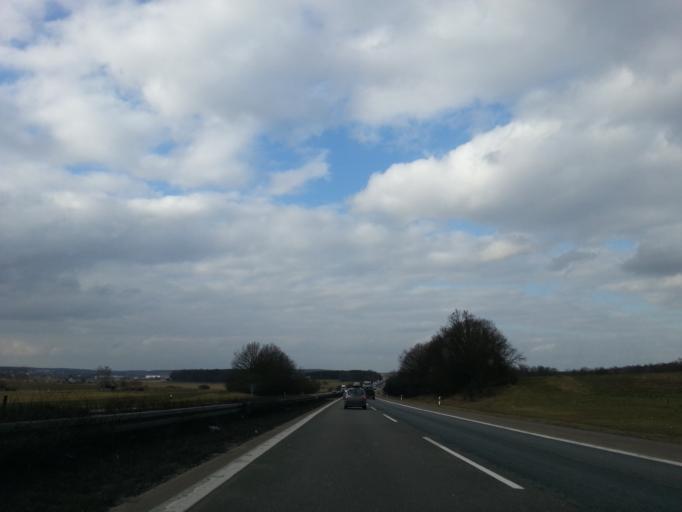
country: DE
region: Bavaria
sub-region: Regierungsbezirk Mittelfranken
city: Gremsdorf
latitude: 49.6845
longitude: 10.8633
